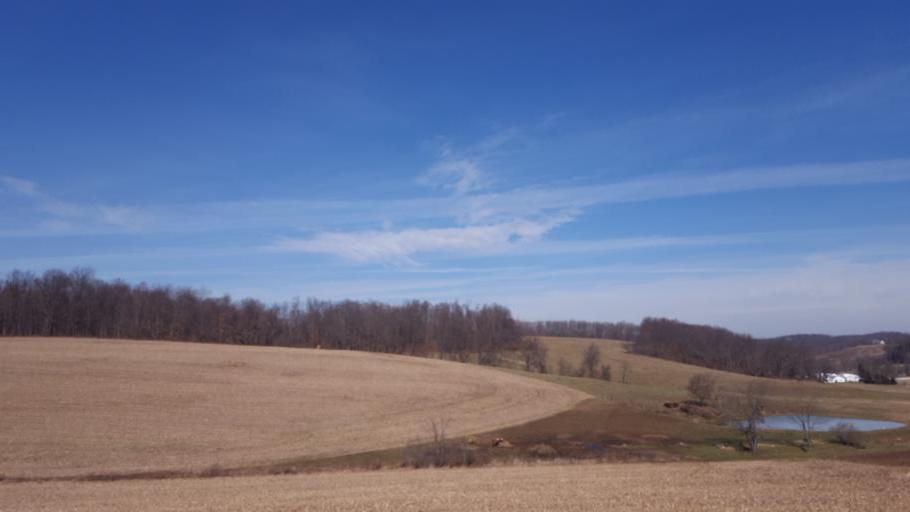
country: US
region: Ohio
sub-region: Sandusky County
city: Bellville
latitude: 40.5486
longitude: -82.3979
